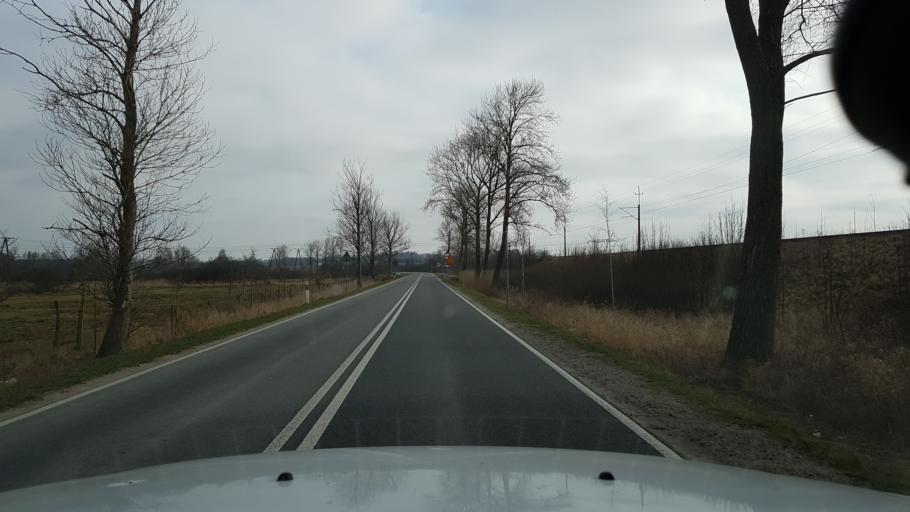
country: PL
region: West Pomeranian Voivodeship
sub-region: Powiat koszalinski
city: Sianow
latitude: 54.2336
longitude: 16.2690
